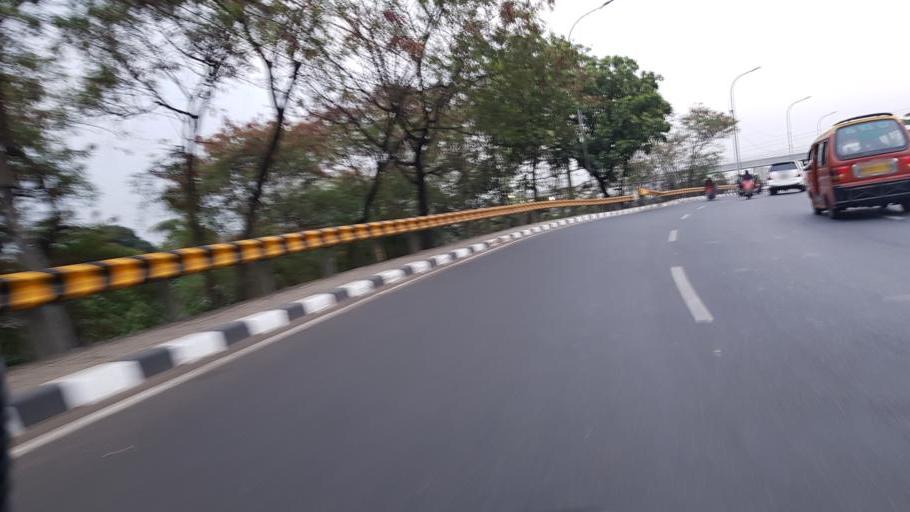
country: ID
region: Jakarta Raya
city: Jakarta
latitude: -6.3075
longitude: 106.8858
